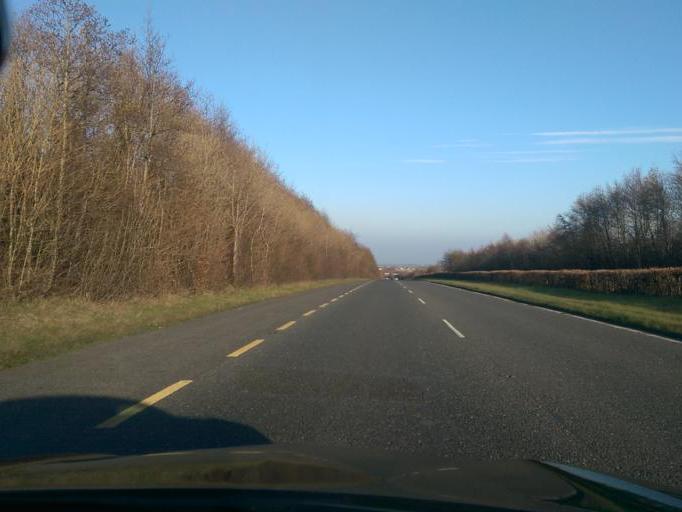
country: IE
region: Connaught
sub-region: County Galway
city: Oranmore
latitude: 53.2791
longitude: -8.9649
